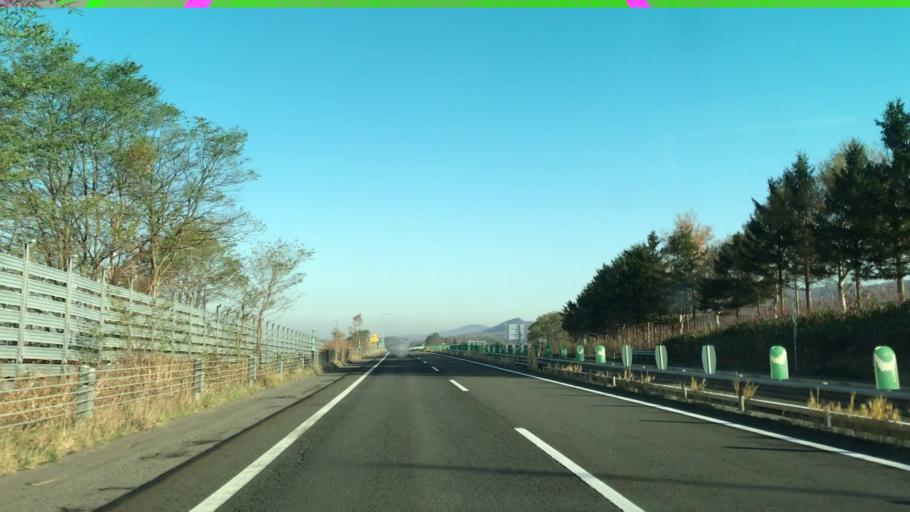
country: JP
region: Hokkaido
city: Sunagawa
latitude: 43.4354
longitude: 141.9154
